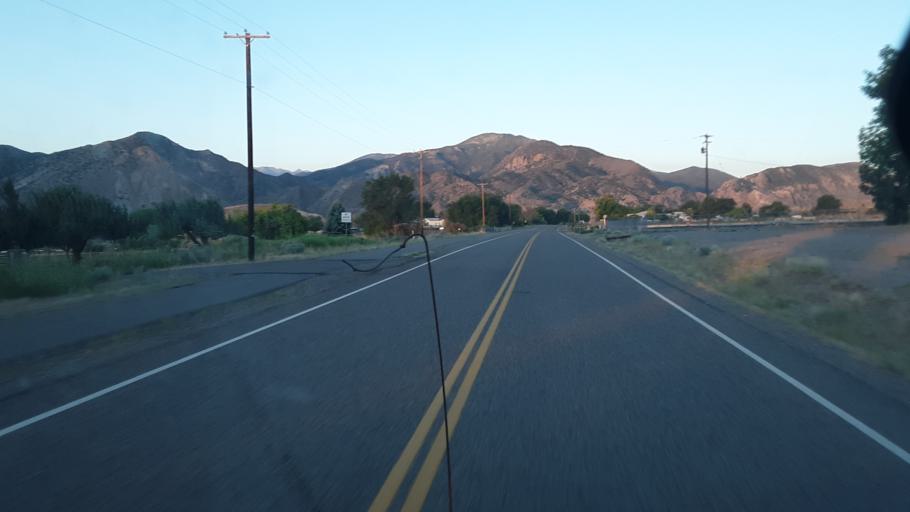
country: US
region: Utah
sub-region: Sevier County
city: Monroe
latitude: 38.5958
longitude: -112.2493
